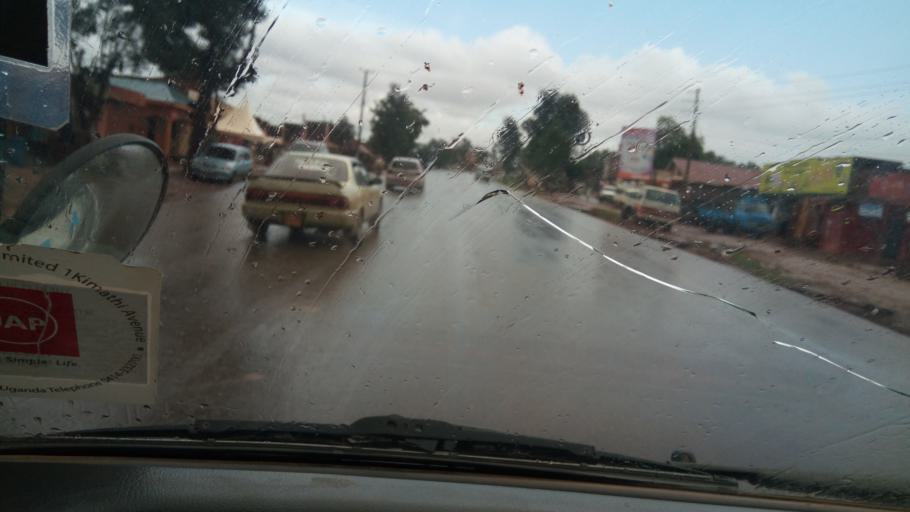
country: UG
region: Central Region
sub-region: Wakiso District
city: Wakiso
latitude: 0.3847
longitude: 32.5162
